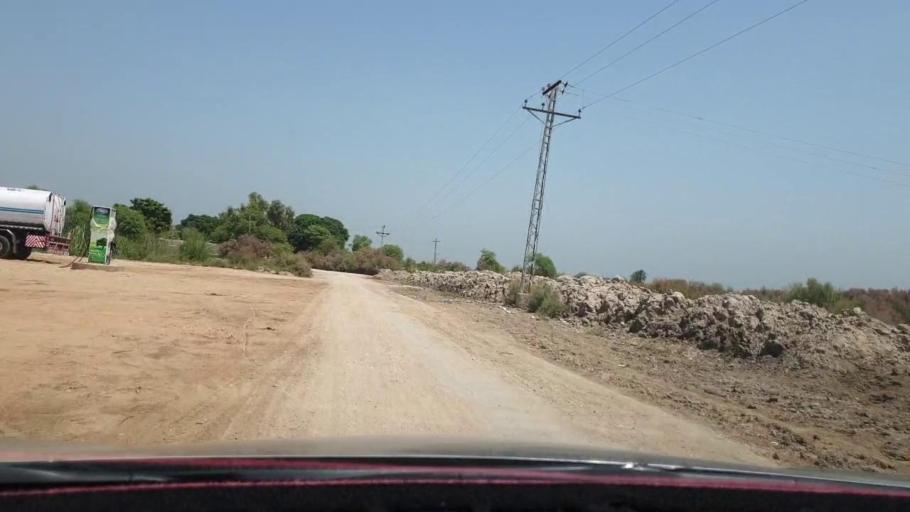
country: PK
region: Sindh
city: Warah
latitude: 27.4348
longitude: 67.7194
